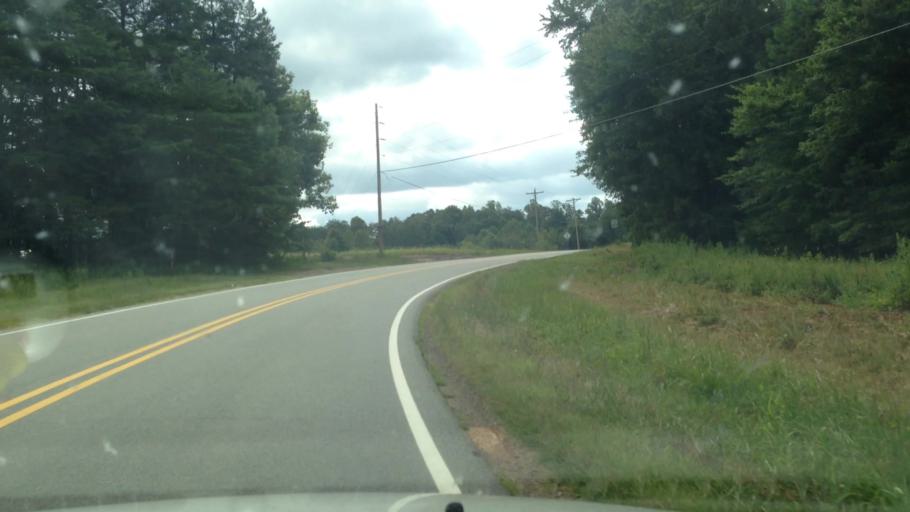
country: US
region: North Carolina
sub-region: Rockingham County
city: Mayodan
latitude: 36.3954
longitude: -80.0174
